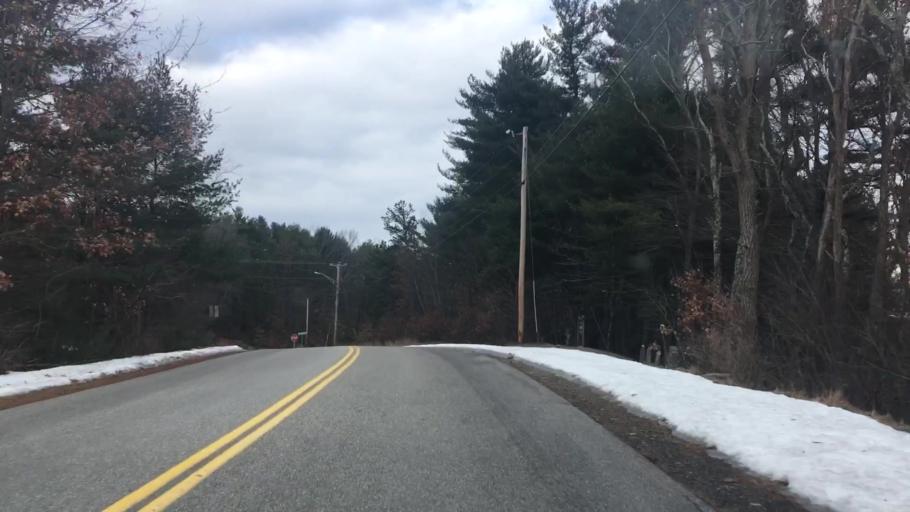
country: US
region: Maine
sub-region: York County
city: Wells Beach Station
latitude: 43.3113
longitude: -70.6535
